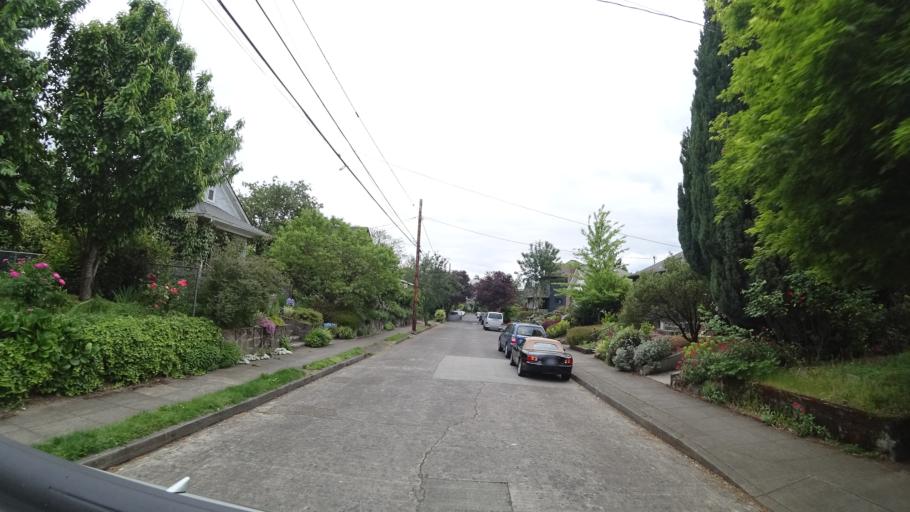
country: US
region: Oregon
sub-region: Multnomah County
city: Lents
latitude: 45.5140
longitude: -122.6142
